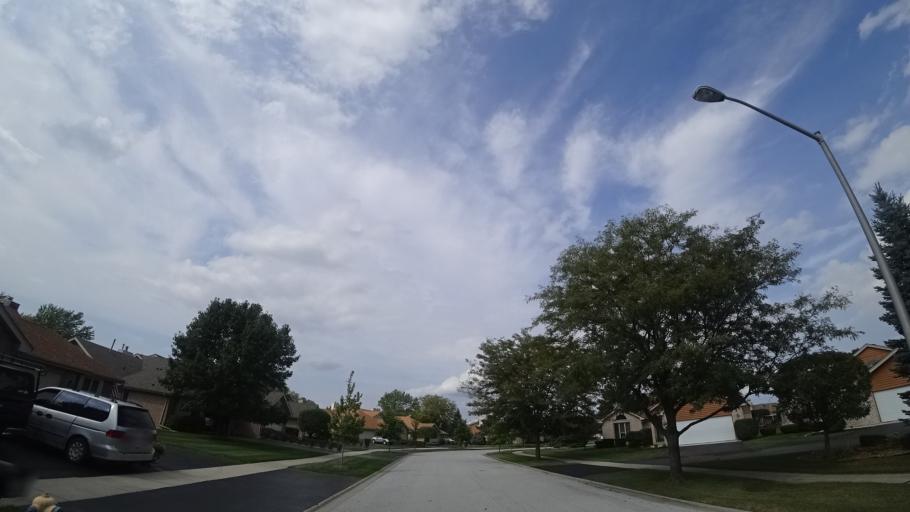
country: US
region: Illinois
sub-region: Cook County
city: Tinley Park
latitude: 41.5571
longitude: -87.7776
